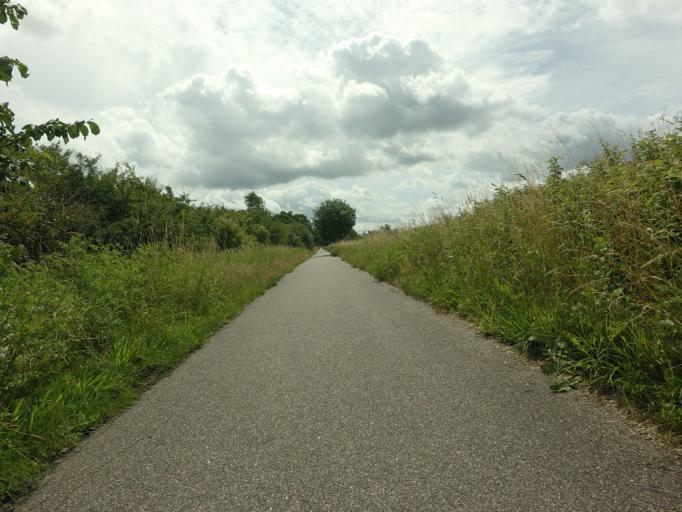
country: DK
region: Central Jutland
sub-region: Randers Kommune
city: Langa
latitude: 56.3760
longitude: 9.8969
